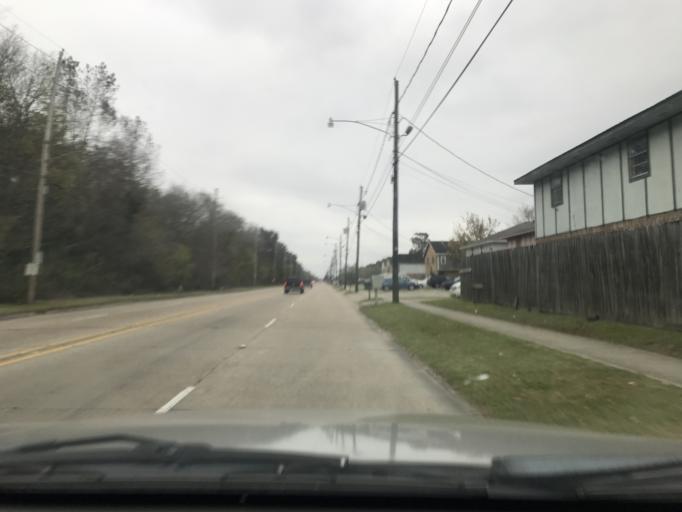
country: US
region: Louisiana
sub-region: Jefferson Parish
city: Woodmere
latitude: 29.8674
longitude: -90.0749
